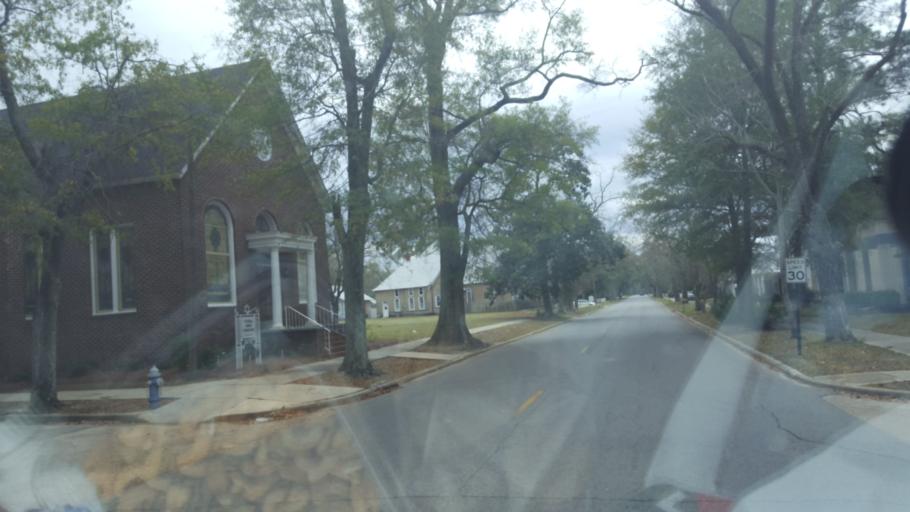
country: US
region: Georgia
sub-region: Ben Hill County
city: Fitzgerald
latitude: 31.7125
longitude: -83.2558
